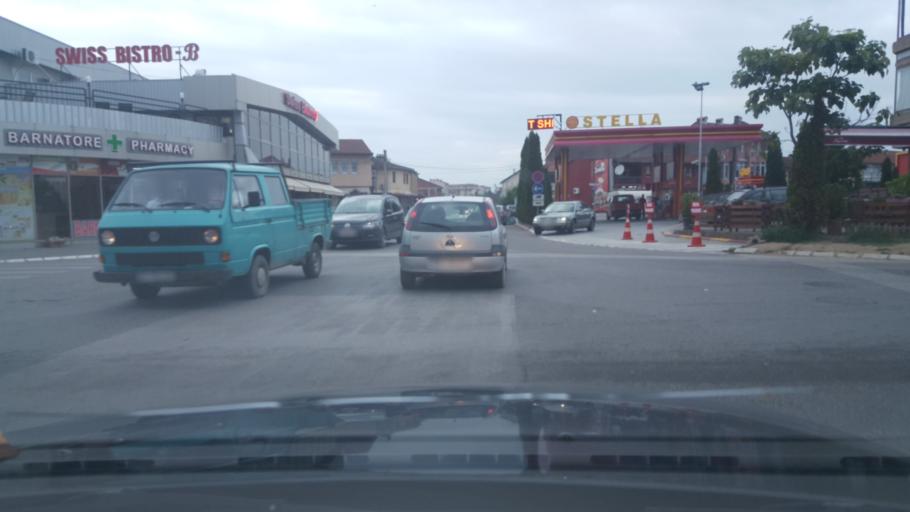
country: XK
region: Gjakova
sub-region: Komuna e Gjakoves
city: Gjakove
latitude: 42.3882
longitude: 20.4321
